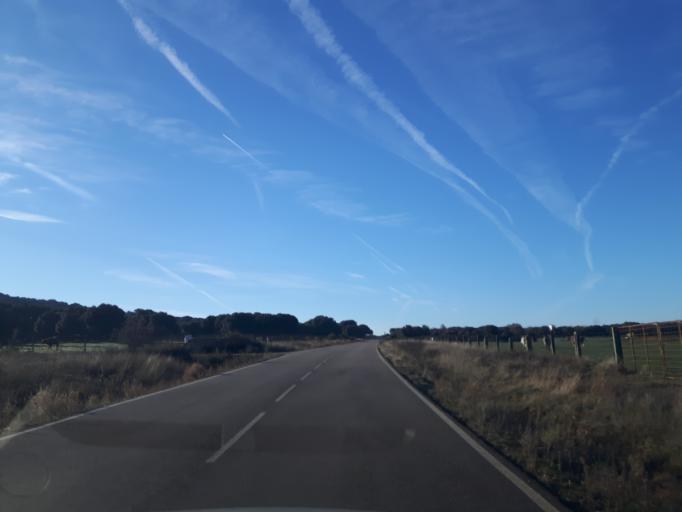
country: ES
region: Castille and Leon
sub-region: Provincia de Salamanca
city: Olmedo de Camaces
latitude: 40.9040
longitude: -6.6190
